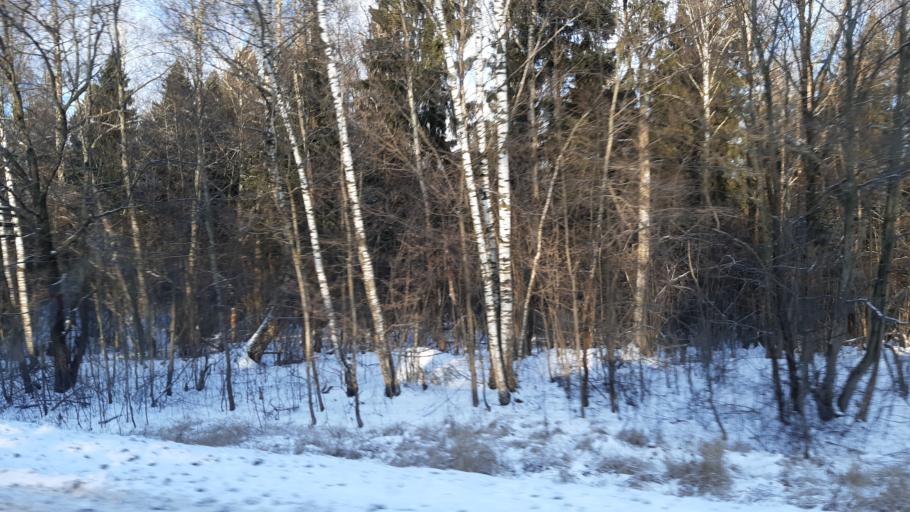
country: RU
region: Moskovskaya
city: Svatkovo
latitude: 56.3008
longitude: 38.3490
